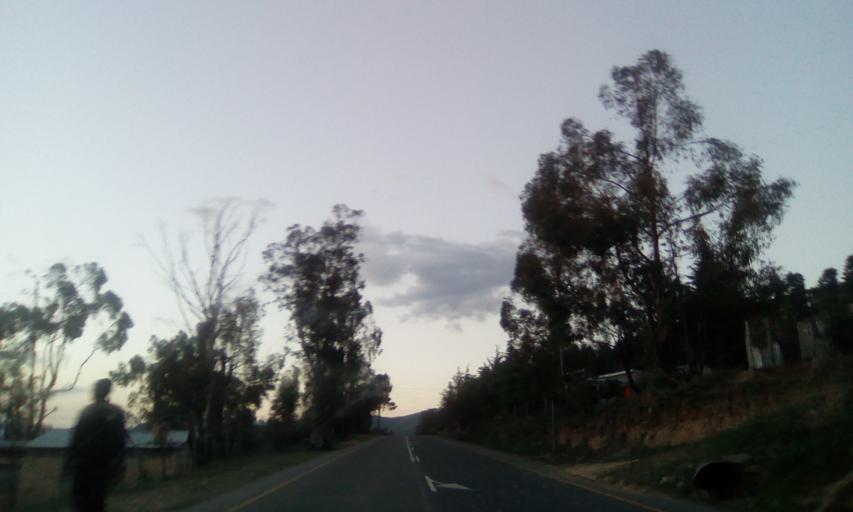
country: LS
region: Qacha's Nek
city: Qacha's Nek
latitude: -30.1258
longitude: 28.6882
